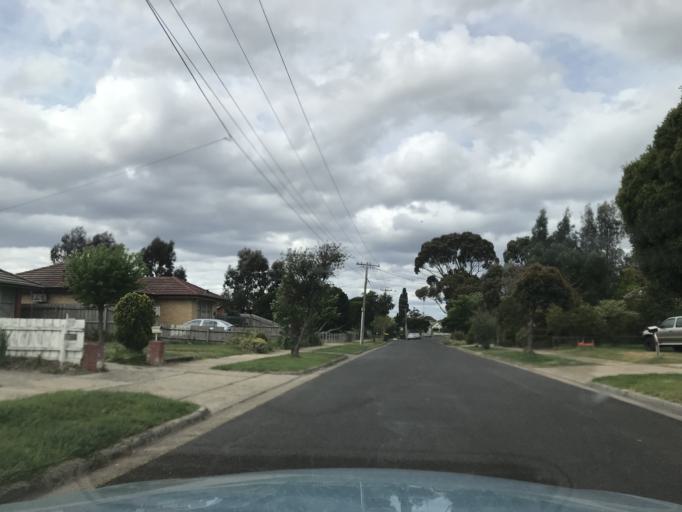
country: AU
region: Victoria
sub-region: Hobsons Bay
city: Laverton
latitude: -37.8504
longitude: 144.7761
